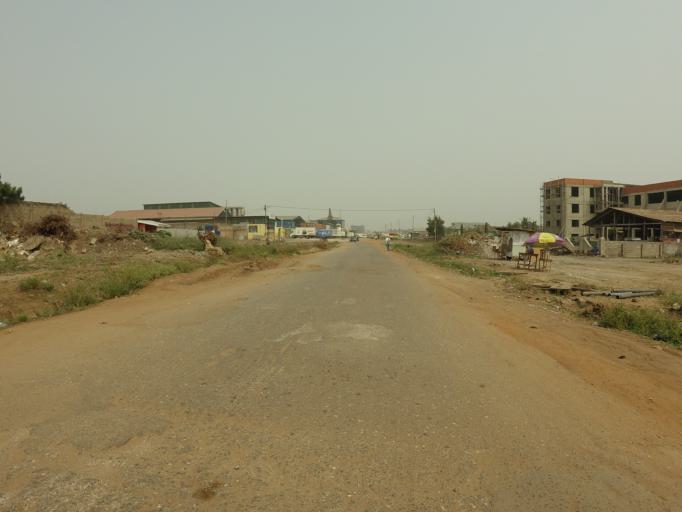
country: GH
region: Greater Accra
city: Nungua
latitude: 5.6438
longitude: -0.1075
